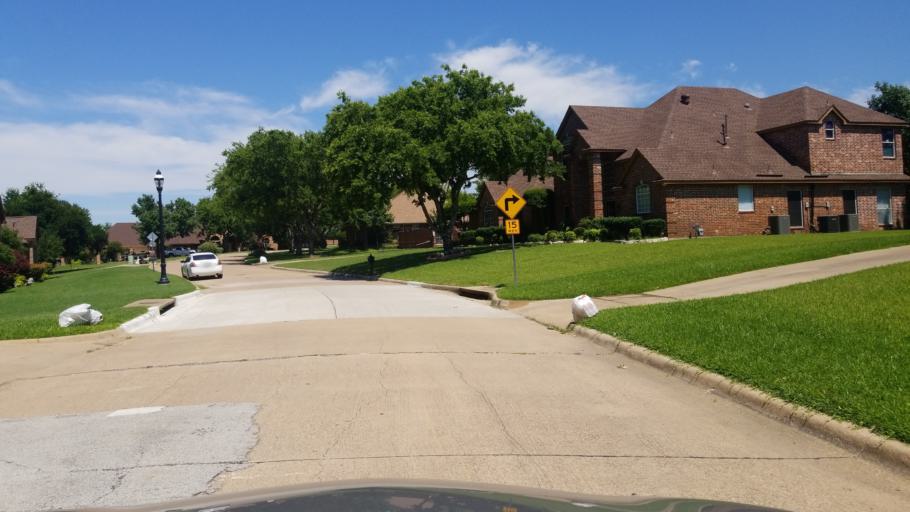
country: US
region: Texas
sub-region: Dallas County
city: Grand Prairie
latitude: 32.6871
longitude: -97.0001
